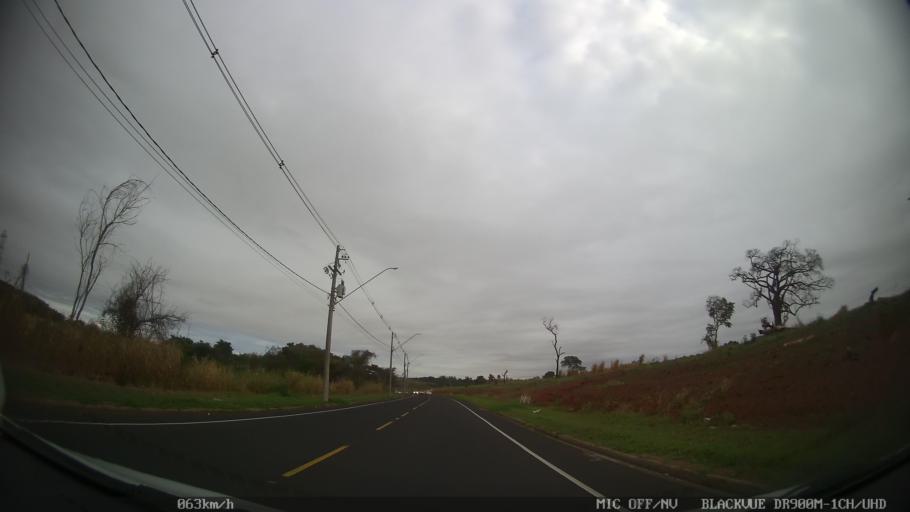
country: BR
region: Sao Paulo
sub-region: Sao Jose Do Rio Preto
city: Sao Jose do Rio Preto
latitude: -20.8289
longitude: -49.4293
